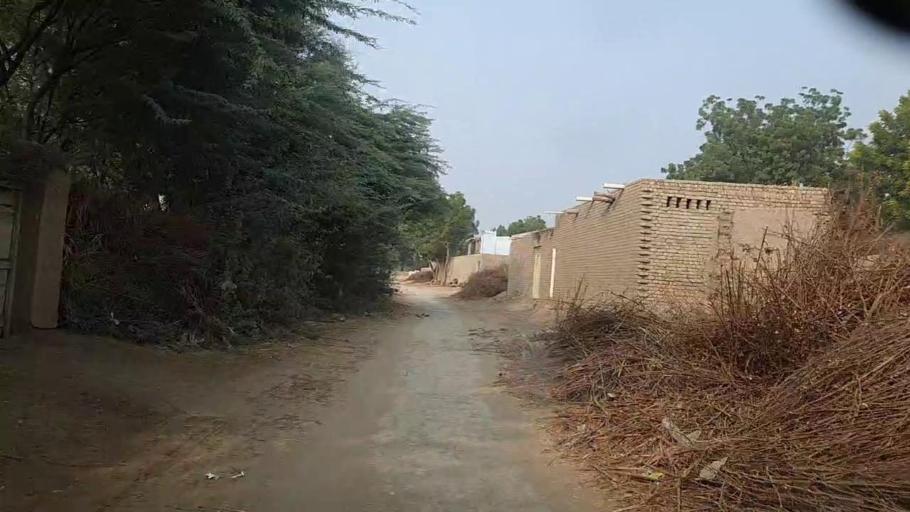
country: PK
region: Sindh
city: Bozdar
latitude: 27.1366
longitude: 68.6617
